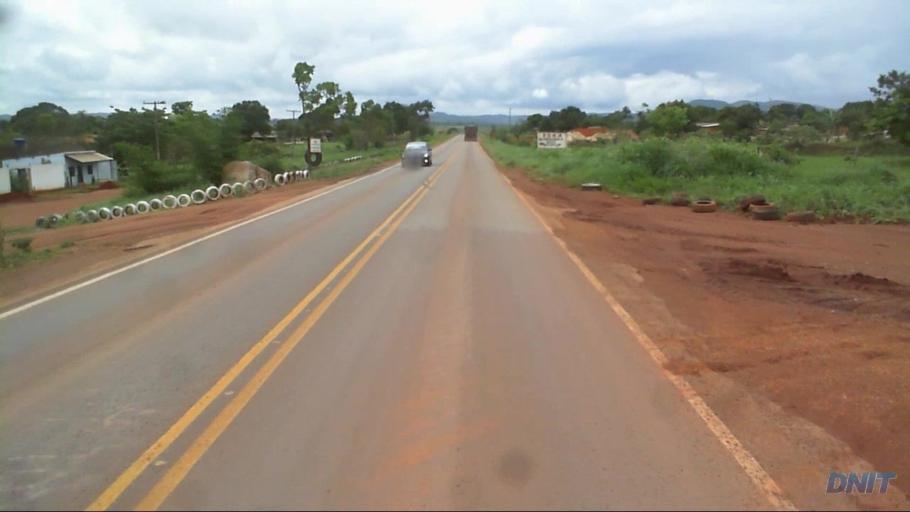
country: BR
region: Goias
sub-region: Padre Bernardo
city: Padre Bernardo
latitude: -15.3640
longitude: -48.2227
